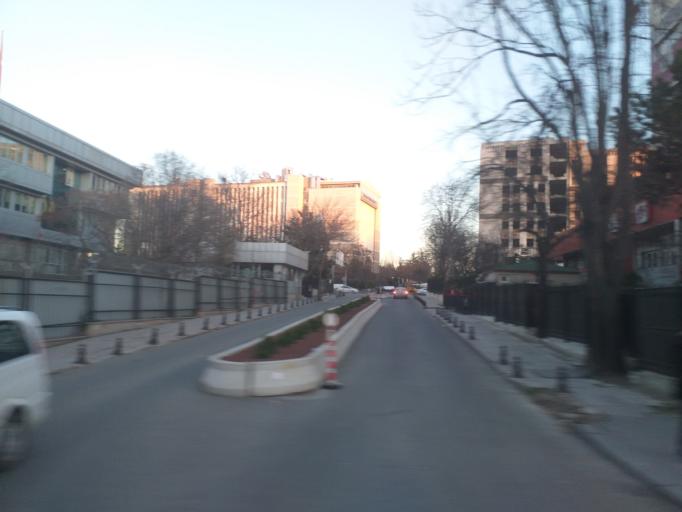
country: TR
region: Ankara
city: Ankara
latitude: 39.9391
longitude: 32.8241
